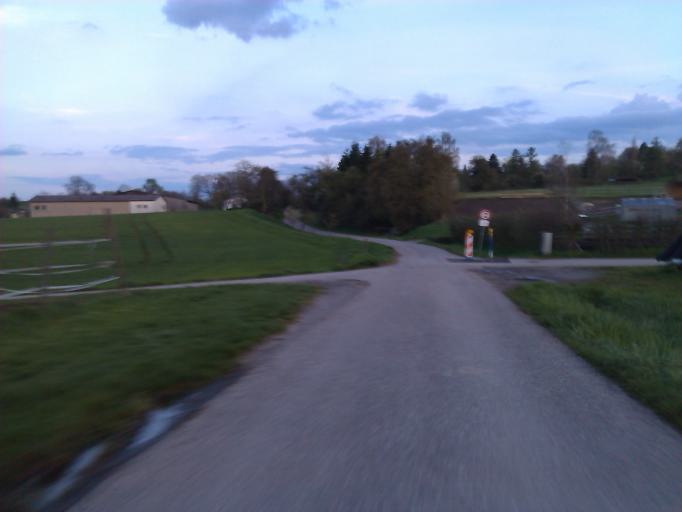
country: DE
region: Baden-Wuerttemberg
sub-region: Regierungsbezirk Stuttgart
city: Bad Wimpfen
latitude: 49.2223
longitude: 9.1715
